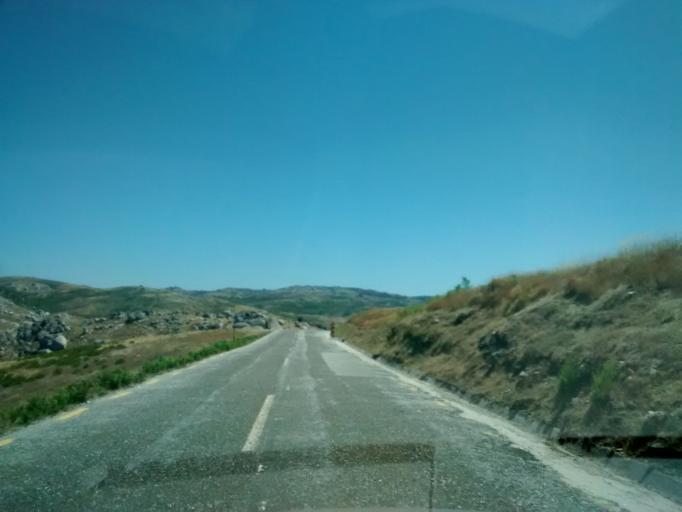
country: PT
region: Guarda
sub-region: Seia
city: Seia
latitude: 40.4210
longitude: -7.6324
